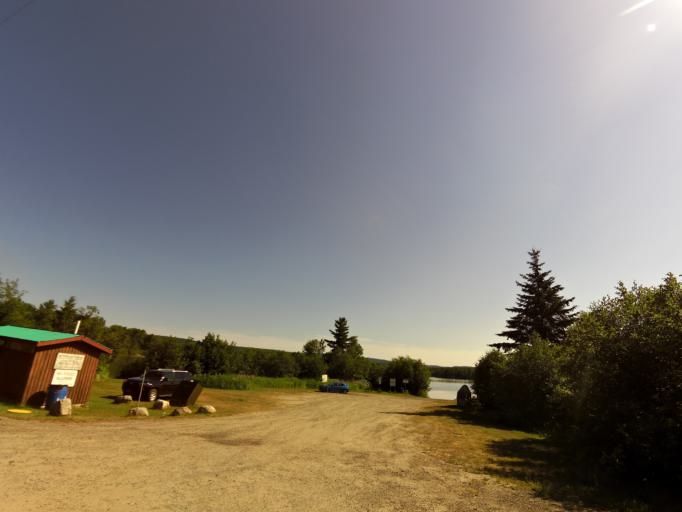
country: CA
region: Ontario
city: Mattawa
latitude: 46.2527
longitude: -78.2879
